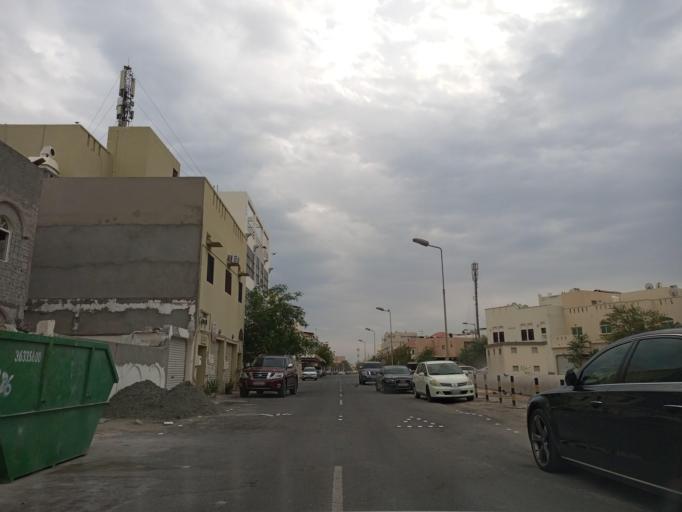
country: BH
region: Muharraq
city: Al Hadd
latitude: 26.2618
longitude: 50.6383
